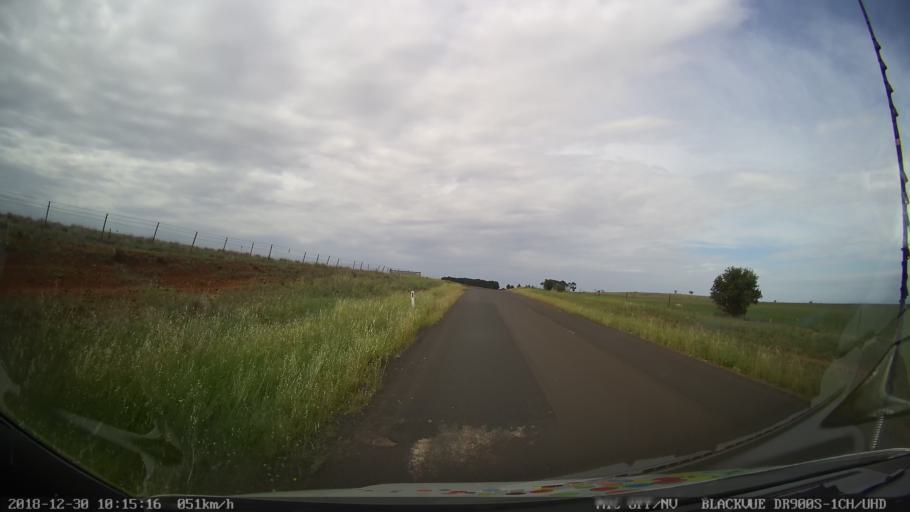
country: AU
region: New South Wales
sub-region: Snowy River
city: Berridale
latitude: -36.5418
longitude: 149.0473
